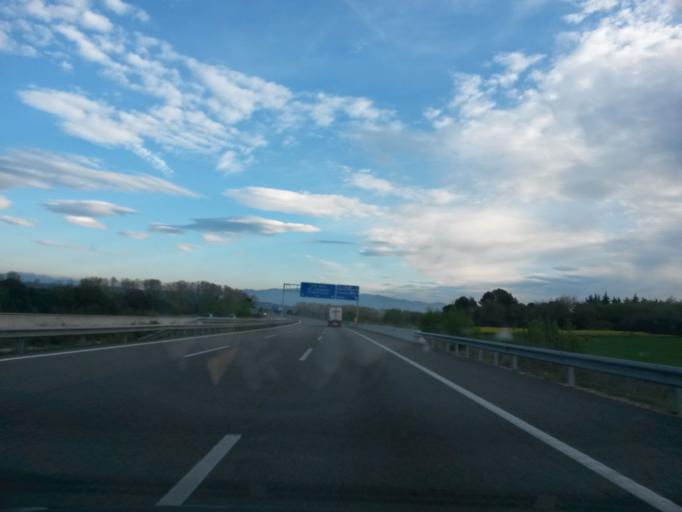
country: ES
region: Catalonia
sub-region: Provincia de Girona
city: Borrassa
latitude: 42.2138
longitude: 2.9404
